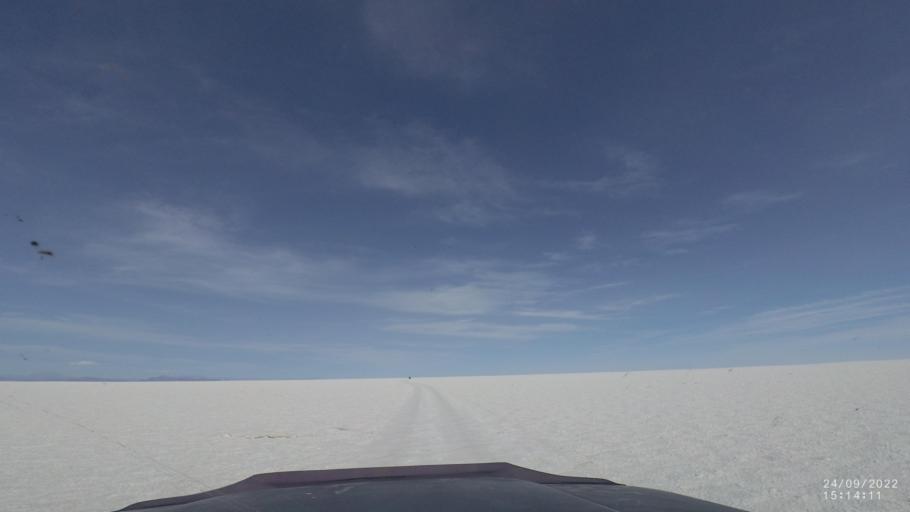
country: BO
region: Potosi
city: Colchani
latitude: -19.9622
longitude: -67.4579
